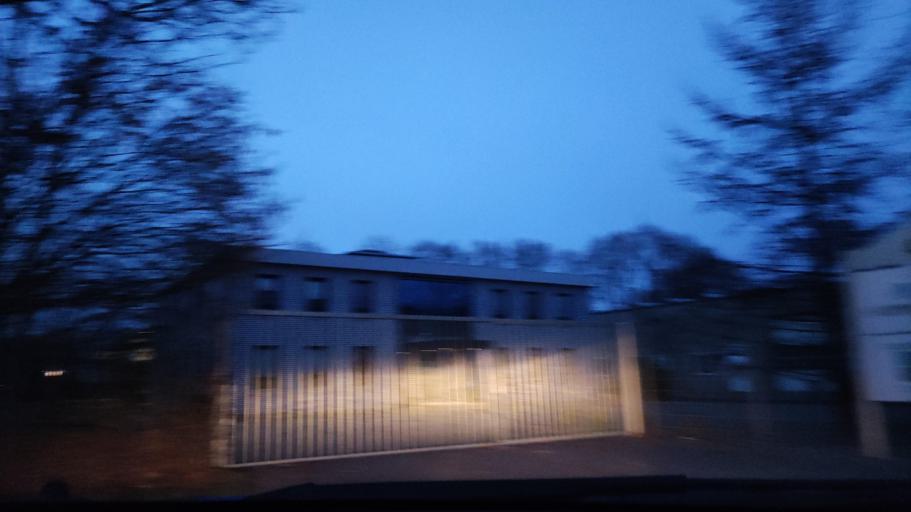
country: DE
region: Schleswig-Holstein
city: Neumunster
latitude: 54.0435
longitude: 9.9873
